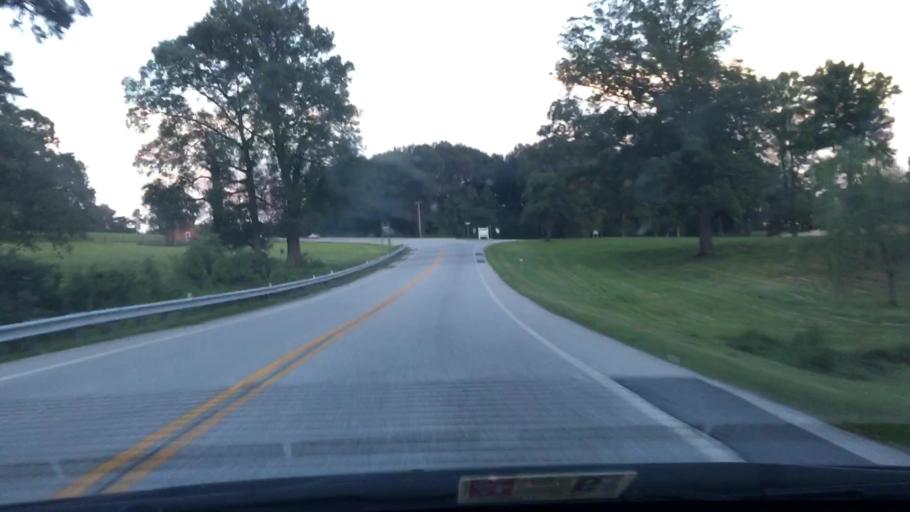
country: US
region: Maryland
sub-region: Prince George's County
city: Greenbelt
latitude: 39.0328
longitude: -76.8782
